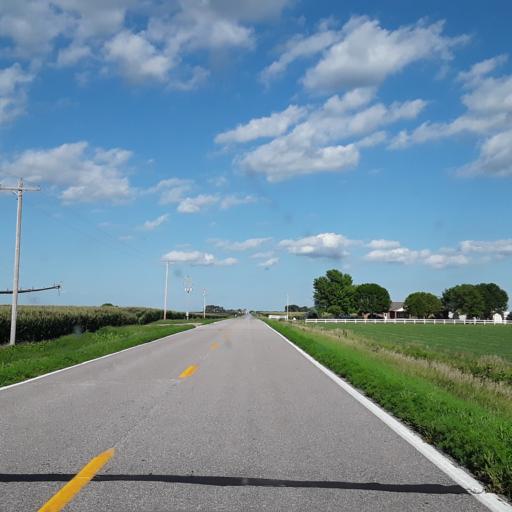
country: US
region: Nebraska
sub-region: Hall County
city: Wood River
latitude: 40.8877
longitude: -98.6232
